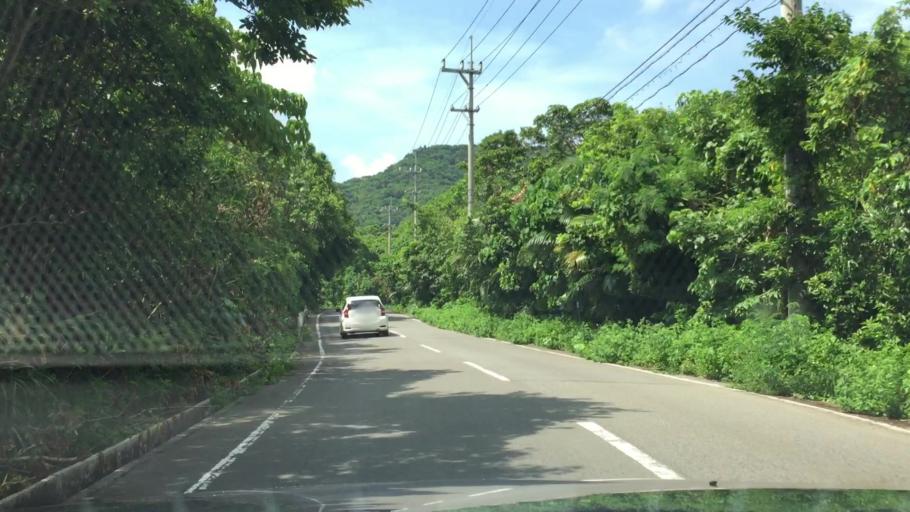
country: JP
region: Okinawa
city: Ishigaki
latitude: 24.4637
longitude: 124.2268
